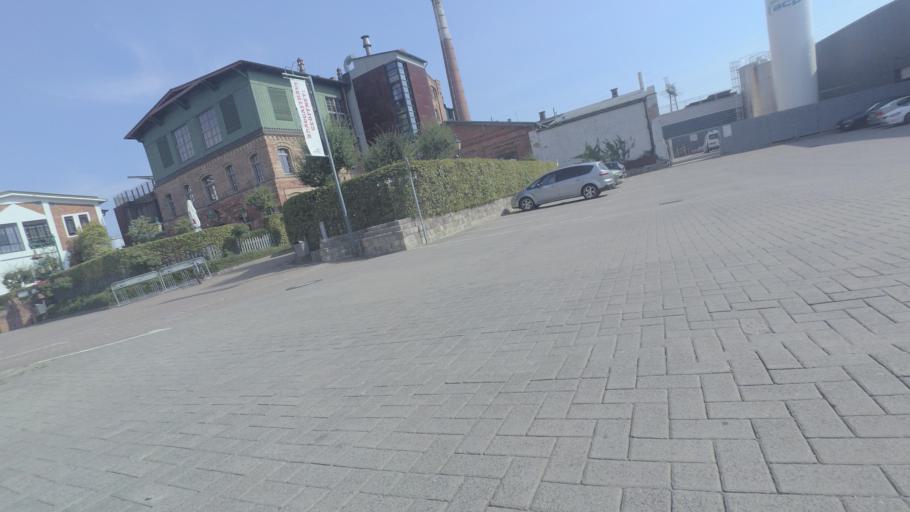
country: DE
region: Mecklenburg-Vorpommern
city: Stralsund
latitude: 54.2902
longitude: 13.0946
